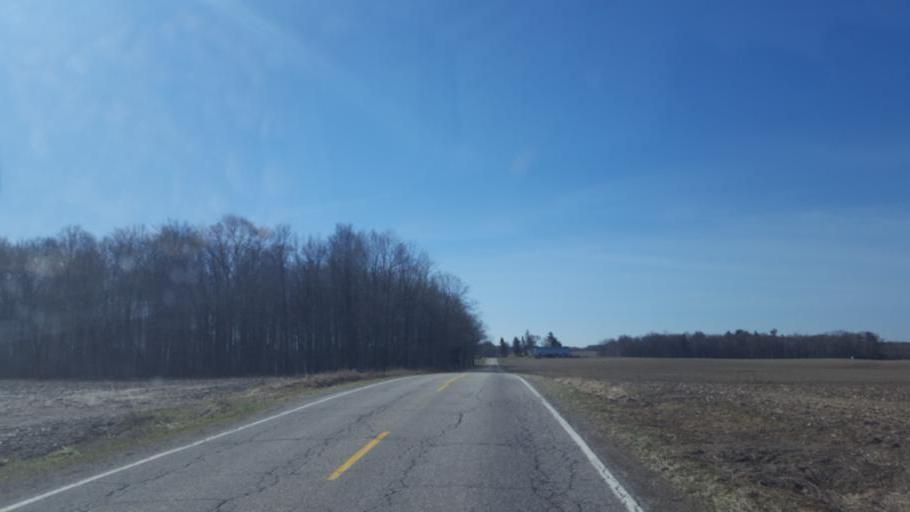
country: US
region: Michigan
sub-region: Montcalm County
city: Edmore
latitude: 43.4960
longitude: -85.0254
